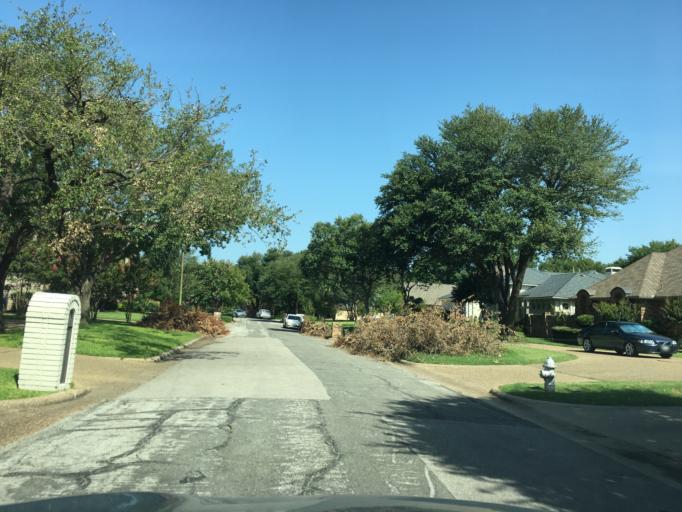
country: US
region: Texas
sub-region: Dallas County
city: Richardson
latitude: 32.9068
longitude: -96.7721
